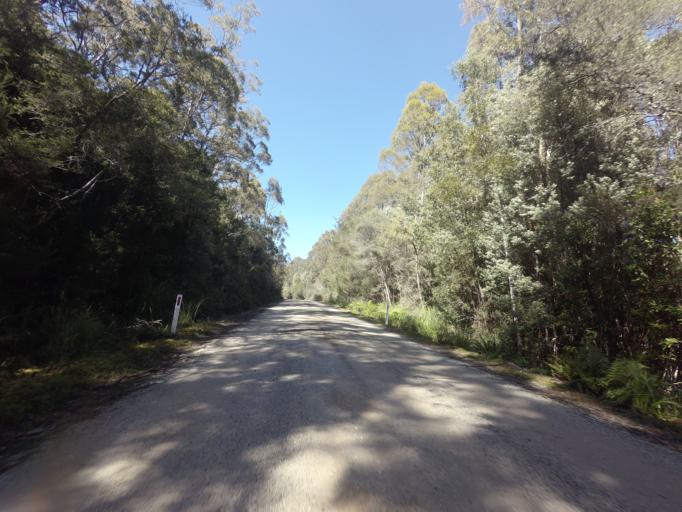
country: AU
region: Tasmania
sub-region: Huon Valley
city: Geeveston
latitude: -43.0130
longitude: 146.3641
